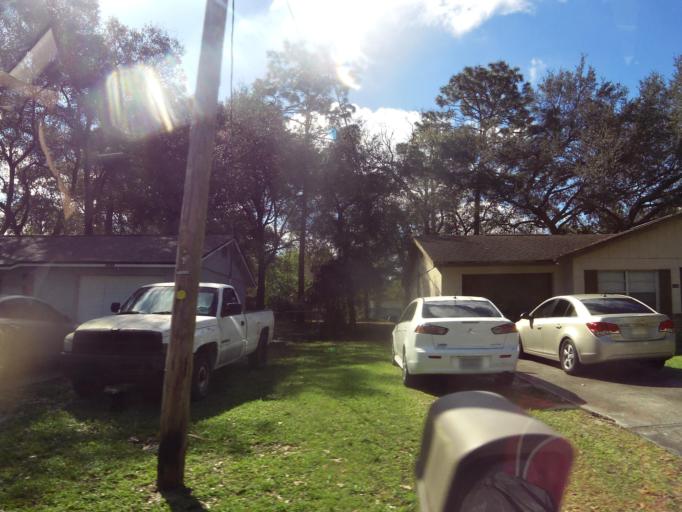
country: US
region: Florida
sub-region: Volusia County
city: Orange City
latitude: 28.9481
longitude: -81.3132
